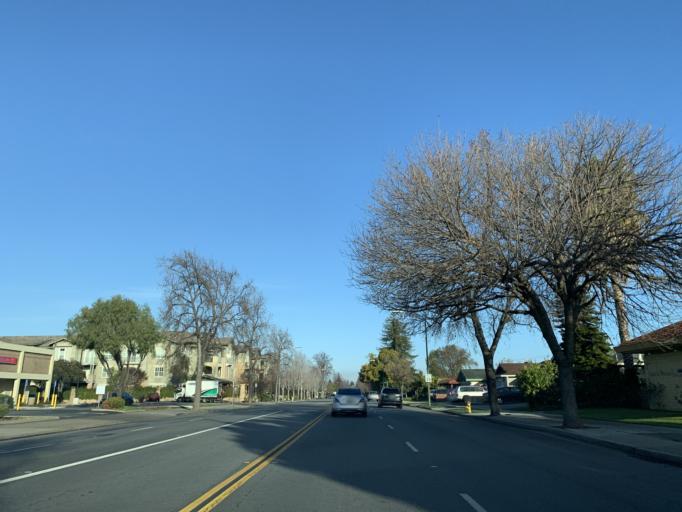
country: US
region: California
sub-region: Santa Clara County
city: Cambrian Park
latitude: 37.2712
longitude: -121.9060
